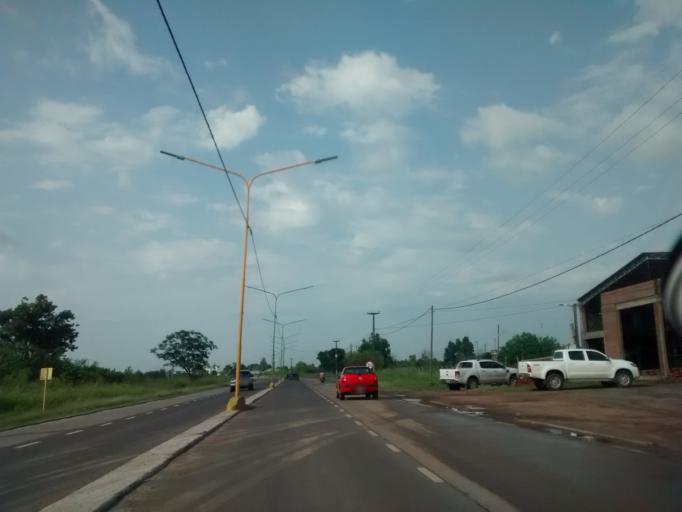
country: AR
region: Chaco
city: Resistencia
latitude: -27.4185
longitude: -58.9720
